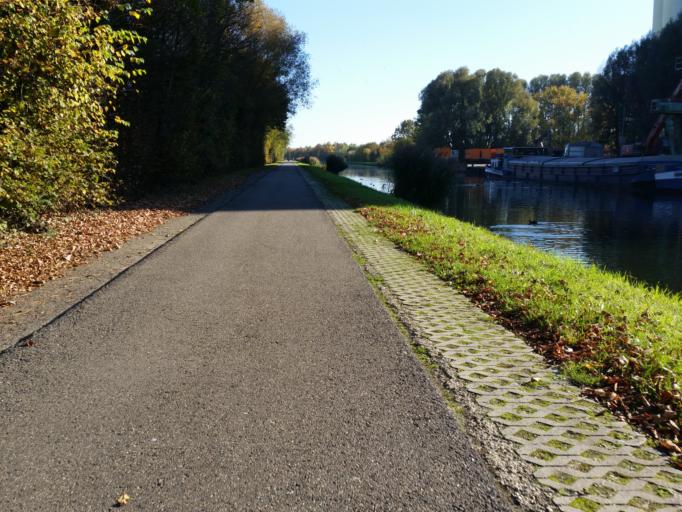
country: BE
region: Flanders
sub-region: Provincie Vlaams-Brabant
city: Herent
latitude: 50.9302
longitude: 4.6801
